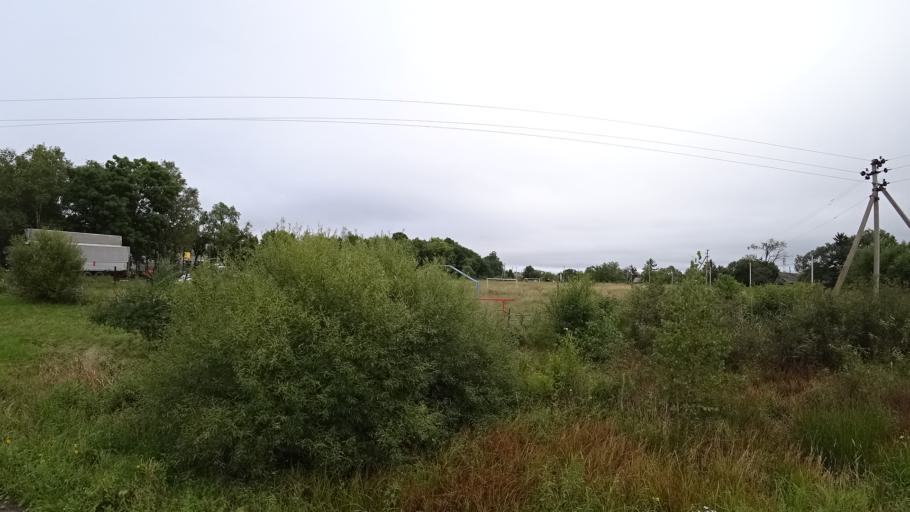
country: RU
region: Primorskiy
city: Monastyrishche
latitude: 44.0820
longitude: 132.5795
